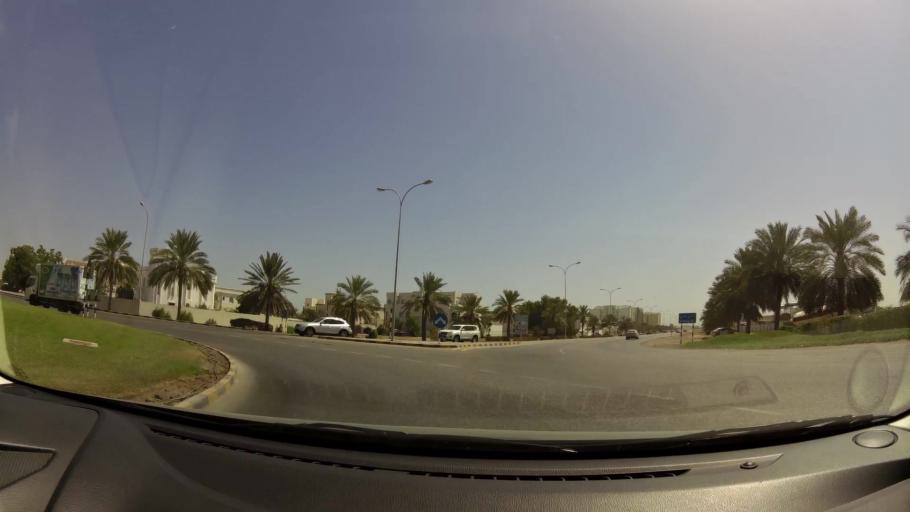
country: OM
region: Muhafazat Masqat
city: As Sib al Jadidah
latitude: 23.6164
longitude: 58.2531
